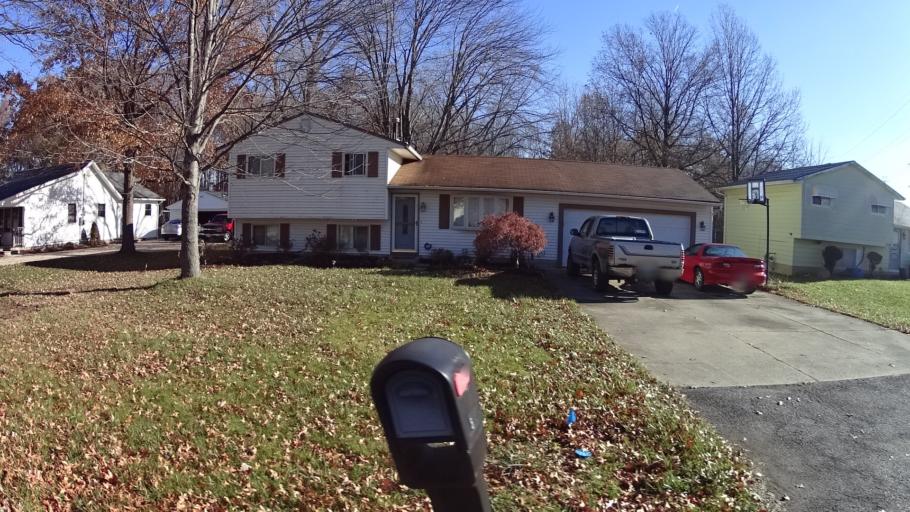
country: US
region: Ohio
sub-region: Lorain County
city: North Ridgeville
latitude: 41.4060
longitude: -81.9974
